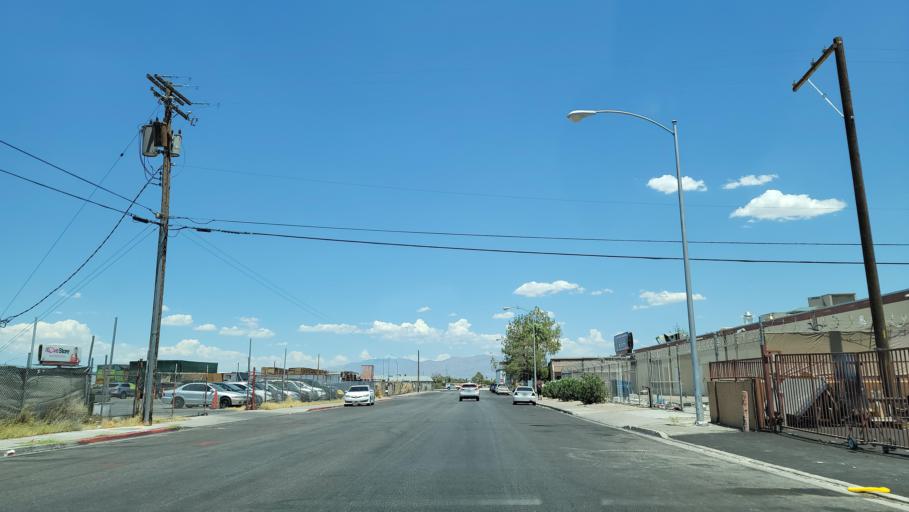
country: US
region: Nevada
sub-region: Clark County
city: Paradise
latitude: 36.1279
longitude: -115.1855
